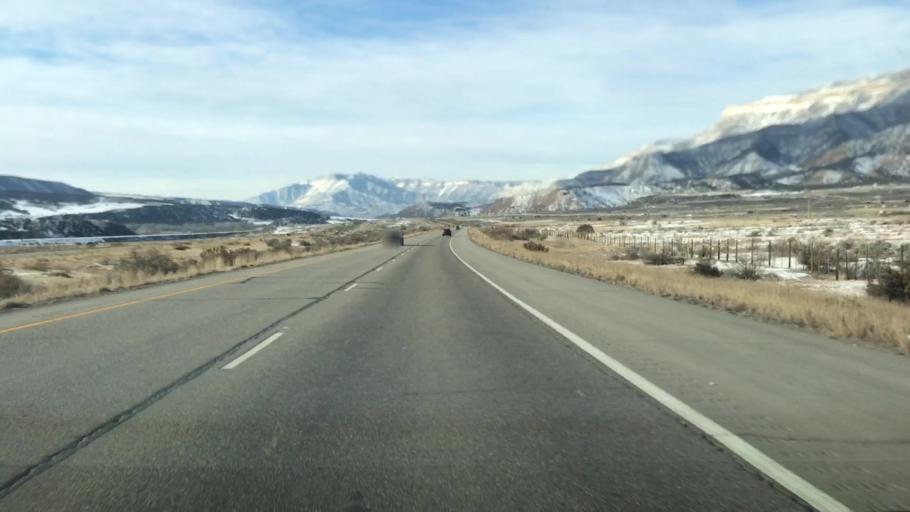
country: US
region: Colorado
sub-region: Garfield County
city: Rifle
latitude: 39.5064
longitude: -107.8877
